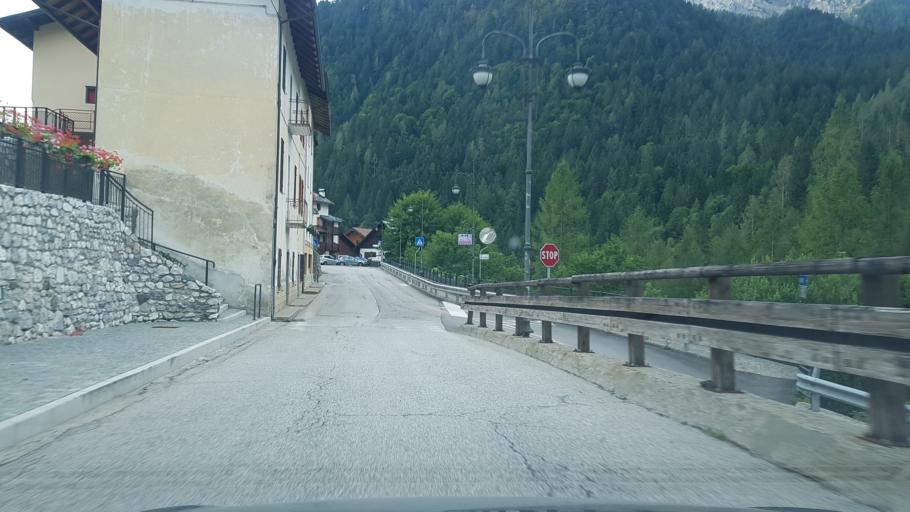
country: IT
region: Friuli Venezia Giulia
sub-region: Provincia di Udine
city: Forni Avoltri
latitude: 46.5860
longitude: 12.7764
